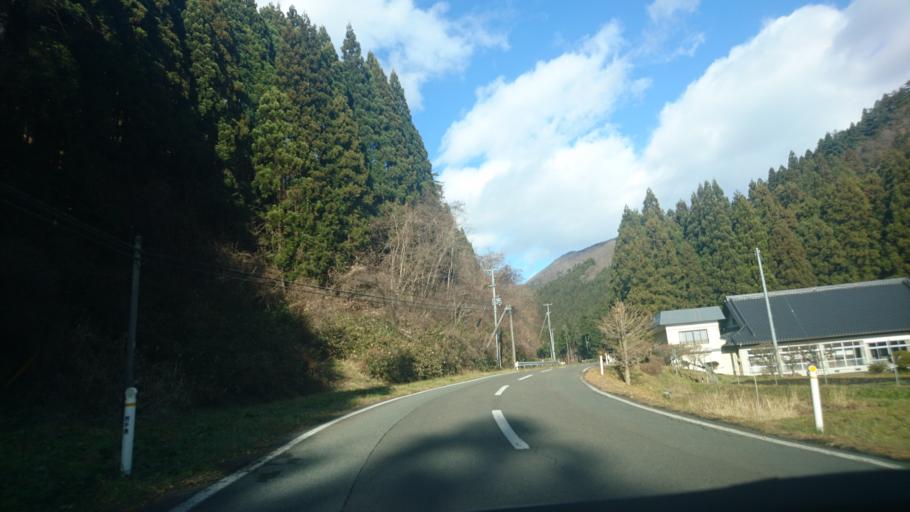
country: JP
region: Iwate
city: Mizusawa
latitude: 39.0775
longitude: 141.3897
